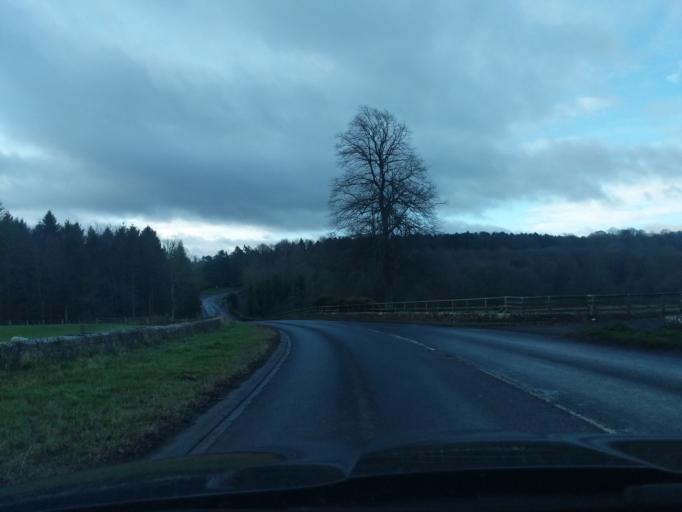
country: GB
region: England
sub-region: Northumberland
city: Alnwick
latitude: 55.4194
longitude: -1.6897
